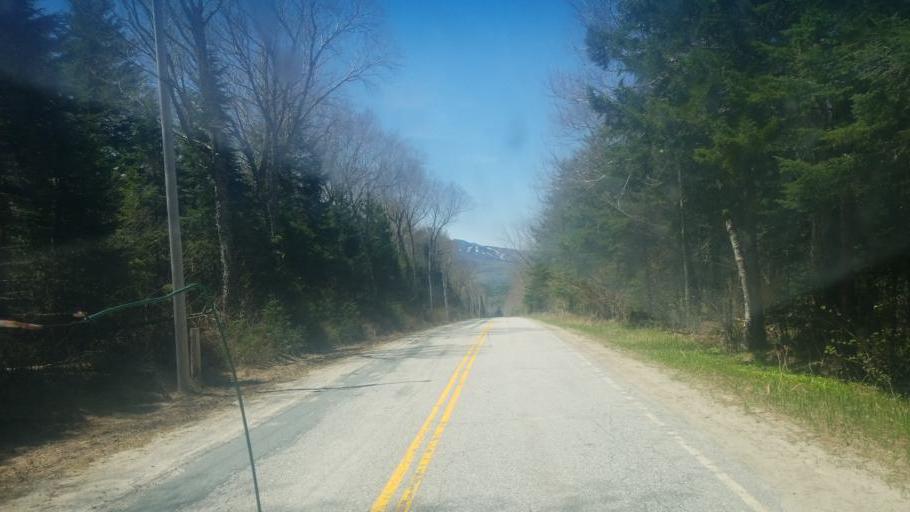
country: US
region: New Hampshire
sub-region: Coos County
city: Jefferson
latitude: 44.2661
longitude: -71.3679
